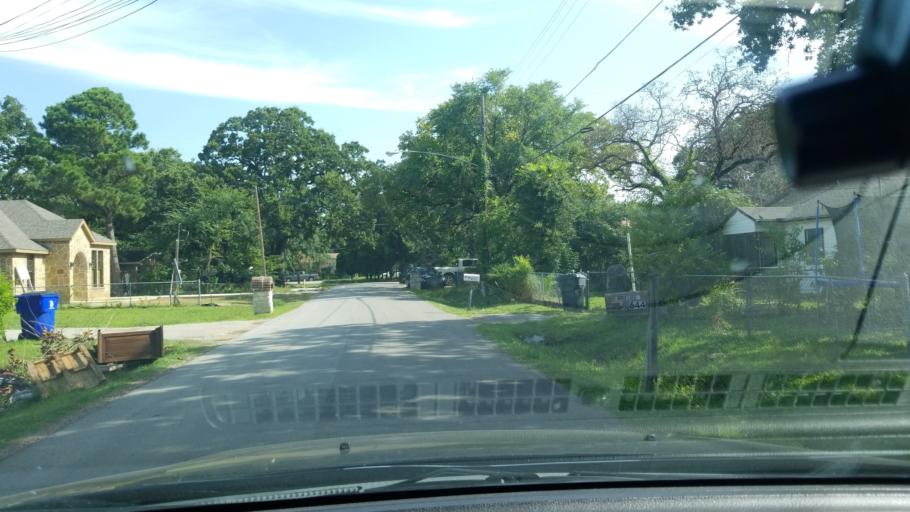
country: US
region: Texas
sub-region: Dallas County
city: Balch Springs
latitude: 32.7231
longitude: -96.6404
